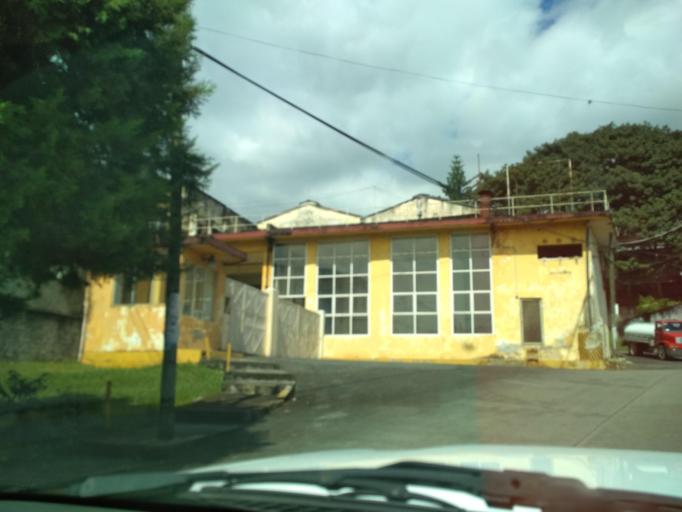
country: MX
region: Veracruz
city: Coatepec
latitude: 19.4518
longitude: -96.9366
